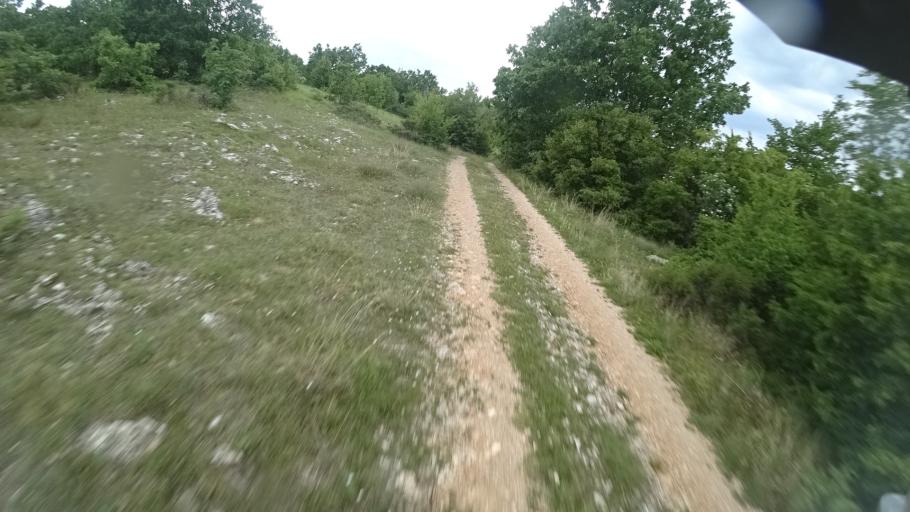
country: HR
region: Sibensko-Kniniska
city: Knin
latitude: 43.9853
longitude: 16.3328
